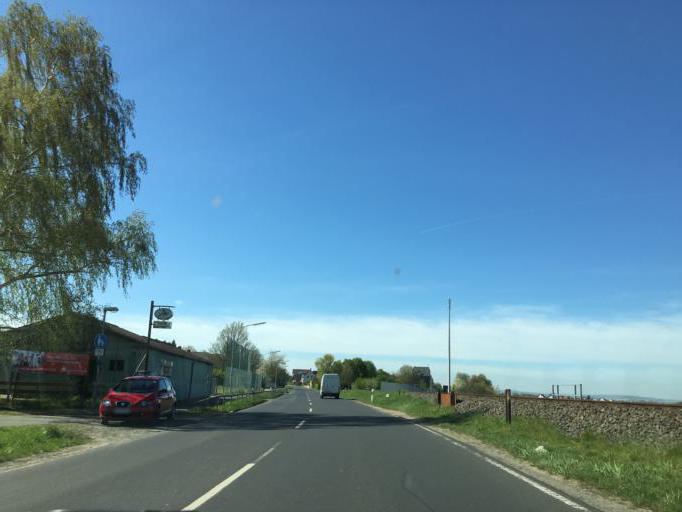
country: DE
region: Hesse
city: Gross-Umstadt
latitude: 49.8970
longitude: 8.9424
